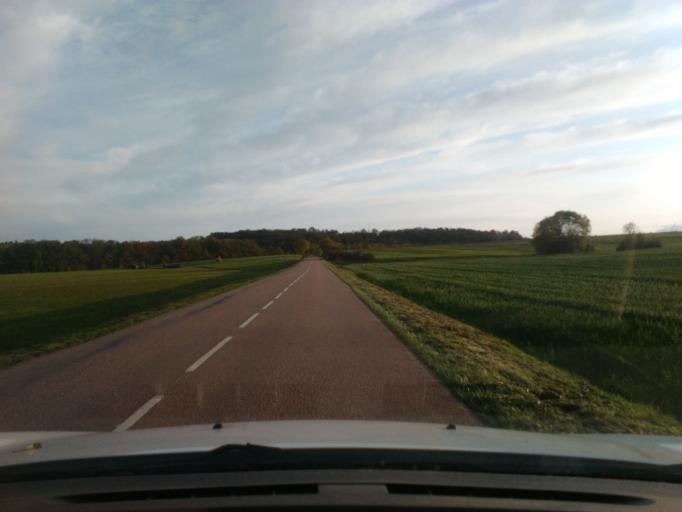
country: FR
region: Lorraine
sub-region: Departement des Vosges
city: Mirecourt
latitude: 48.2221
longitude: 6.1552
